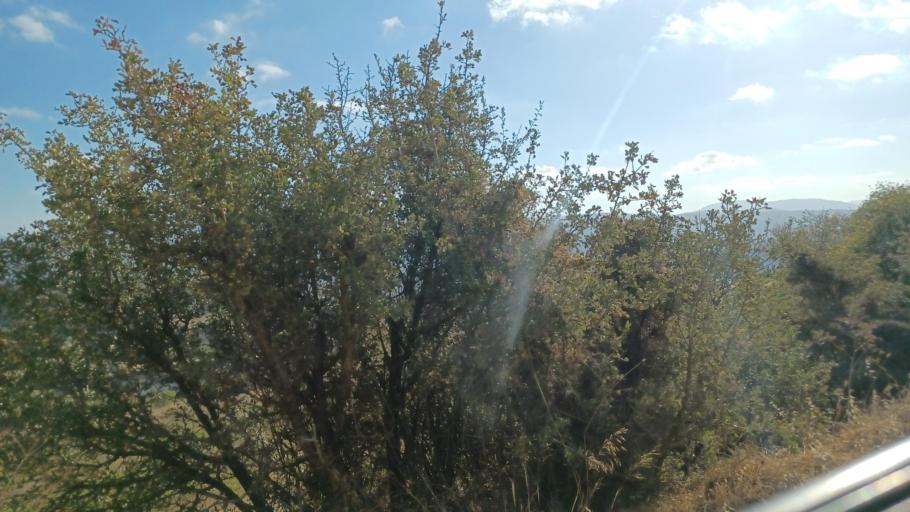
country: CY
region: Pafos
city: Mesogi
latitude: 34.8374
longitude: 32.5256
